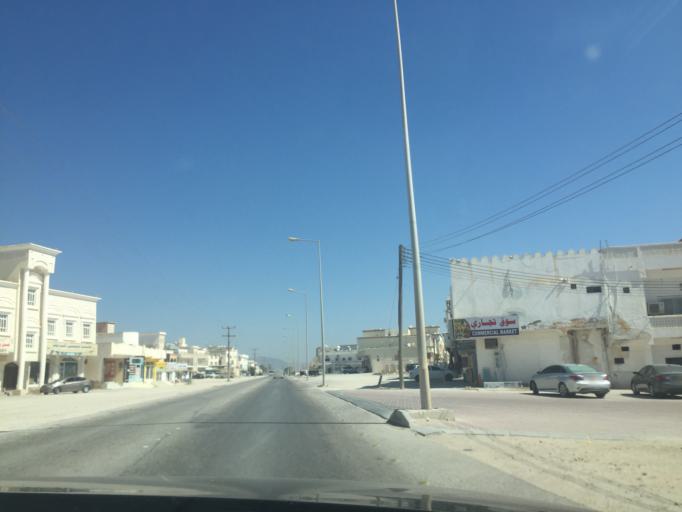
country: OM
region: Zufar
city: Salalah
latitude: 17.0208
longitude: 54.1627
